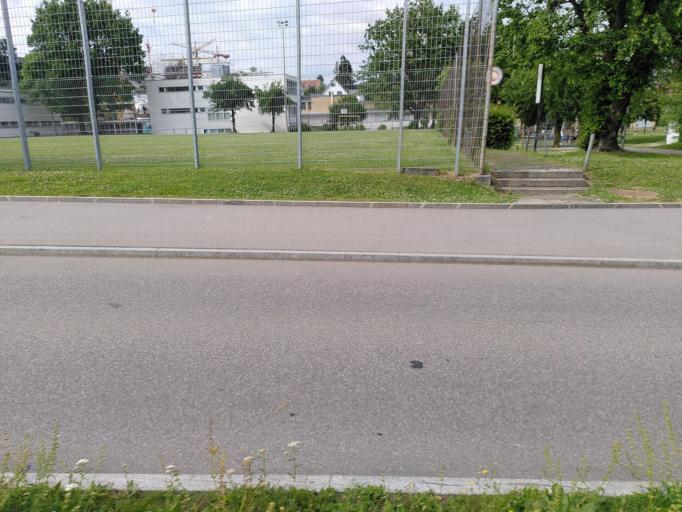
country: CH
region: Zurich
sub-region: Bezirk Horgen
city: Richterswil / Burghalde
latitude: 47.2074
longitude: 8.6903
